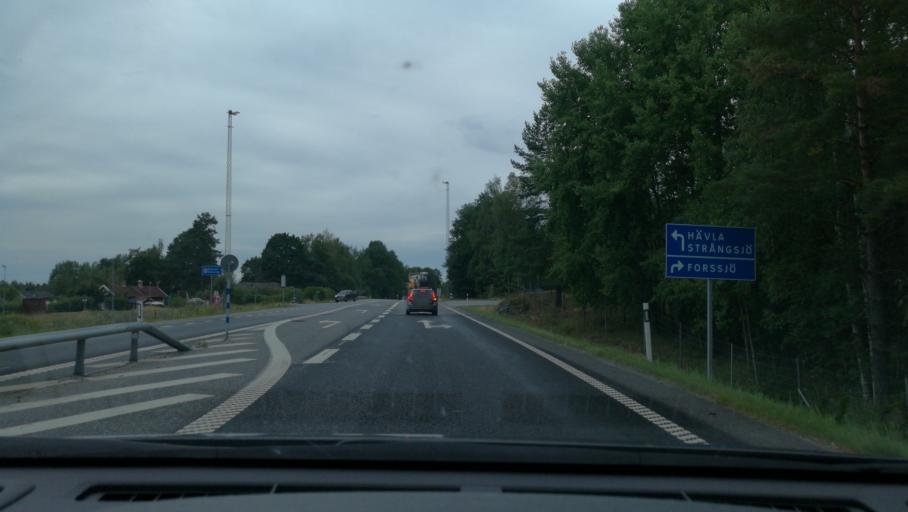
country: SE
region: Soedermanland
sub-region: Katrineholms Kommun
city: Katrineholm
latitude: 58.9042
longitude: 16.2030
